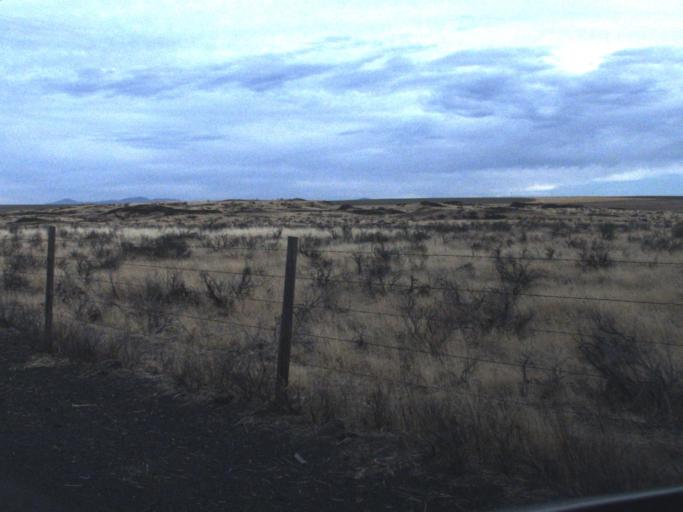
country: US
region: Washington
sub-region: Okanogan County
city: Coulee Dam
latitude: 47.6798
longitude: -118.7218
